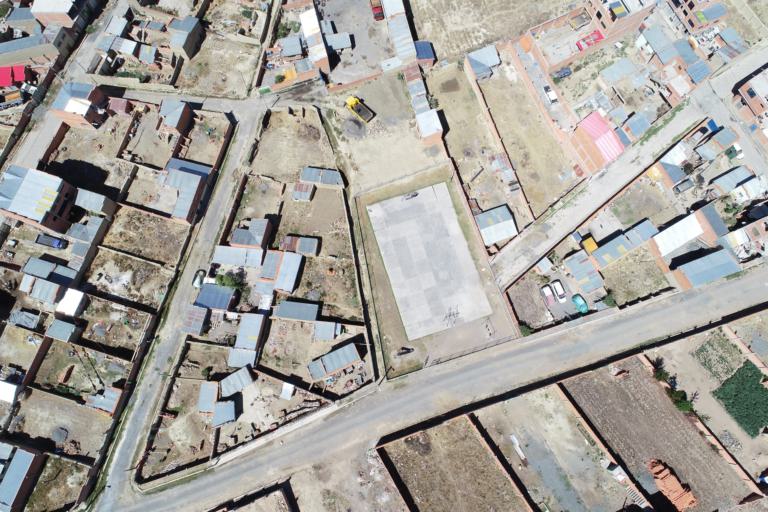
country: BO
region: La Paz
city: Achacachi
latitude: -16.0469
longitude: -68.6796
